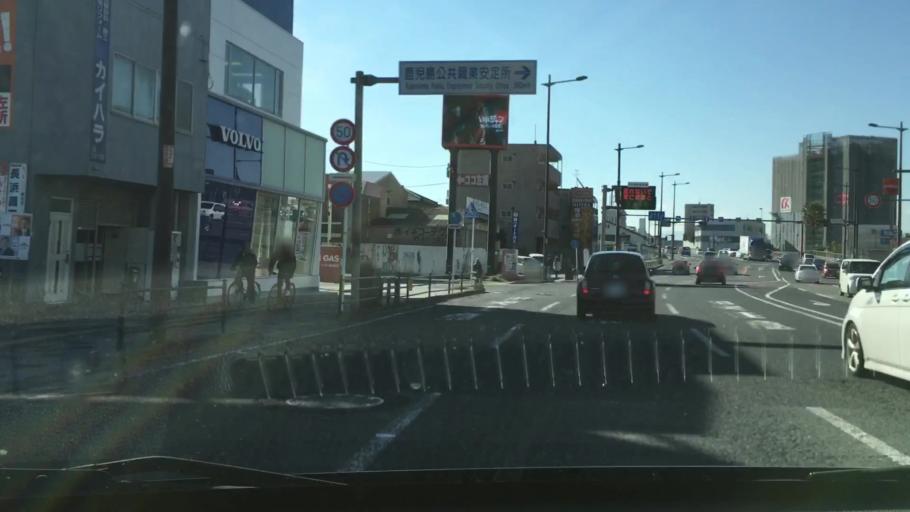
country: JP
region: Kagoshima
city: Kagoshima-shi
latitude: 31.5783
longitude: 130.5623
